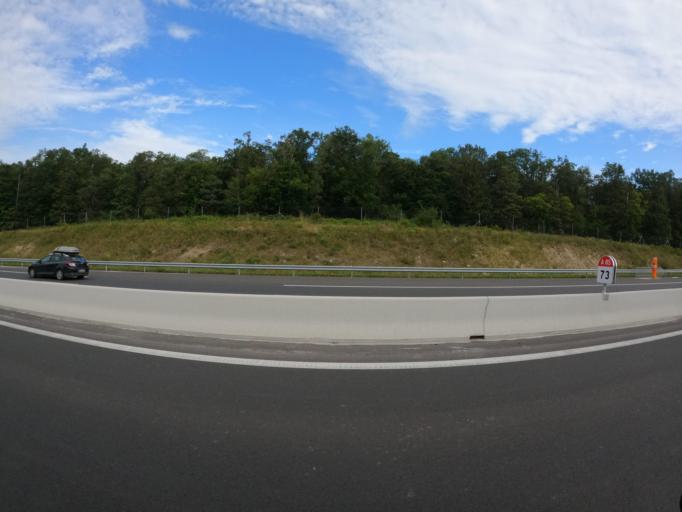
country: FR
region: Centre
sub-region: Departement d'Indre-et-Loire
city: Langeais
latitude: 47.3391
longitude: 0.3527
